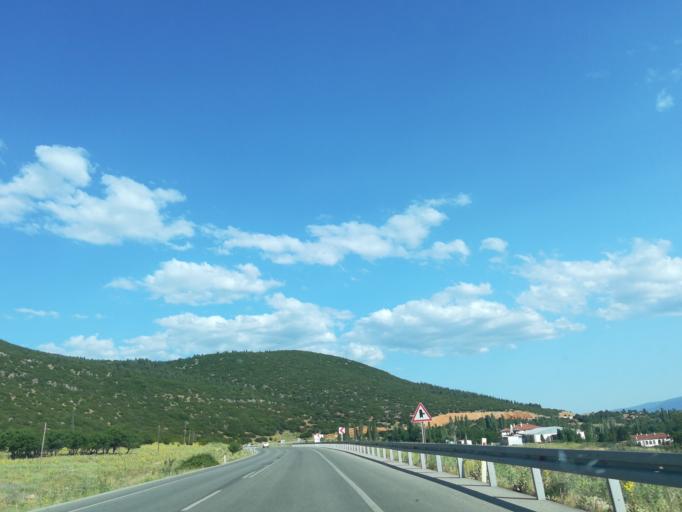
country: TR
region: Denizli
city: Ishakli
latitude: 38.1627
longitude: 30.0780
